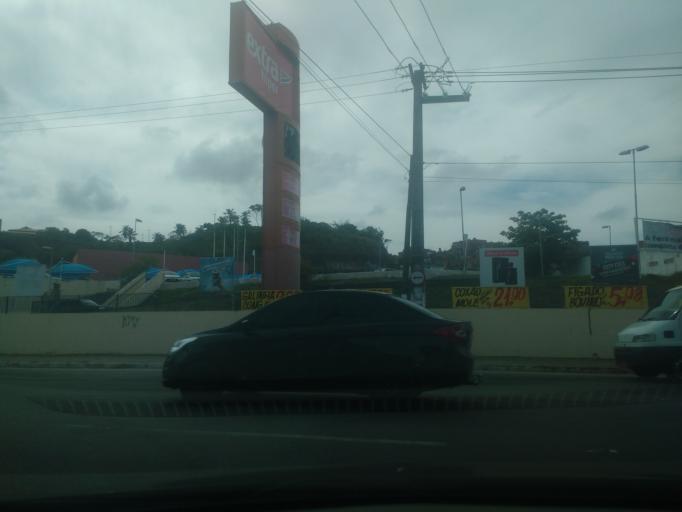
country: BR
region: Alagoas
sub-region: Maceio
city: Maceio
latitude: -9.6456
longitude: -35.7134
